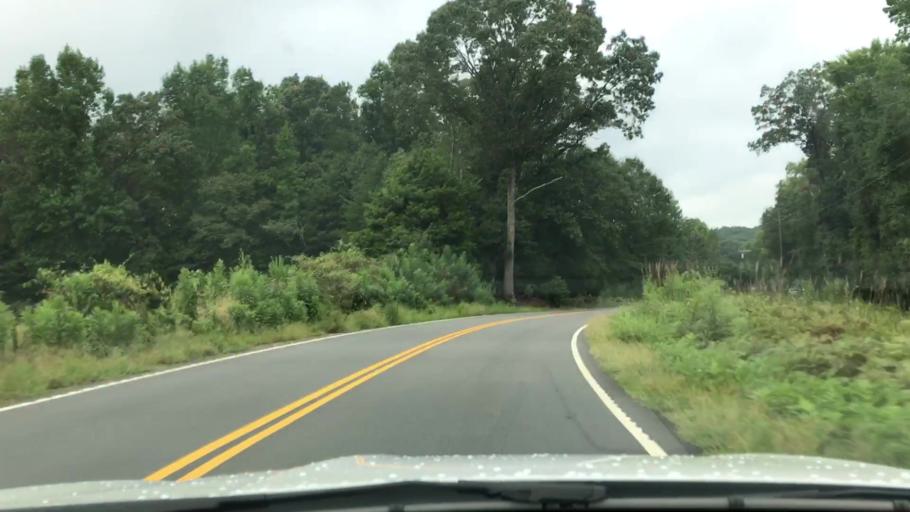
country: US
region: South Carolina
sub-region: Spartanburg County
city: Roebuck
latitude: 34.8218
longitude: -81.9382
